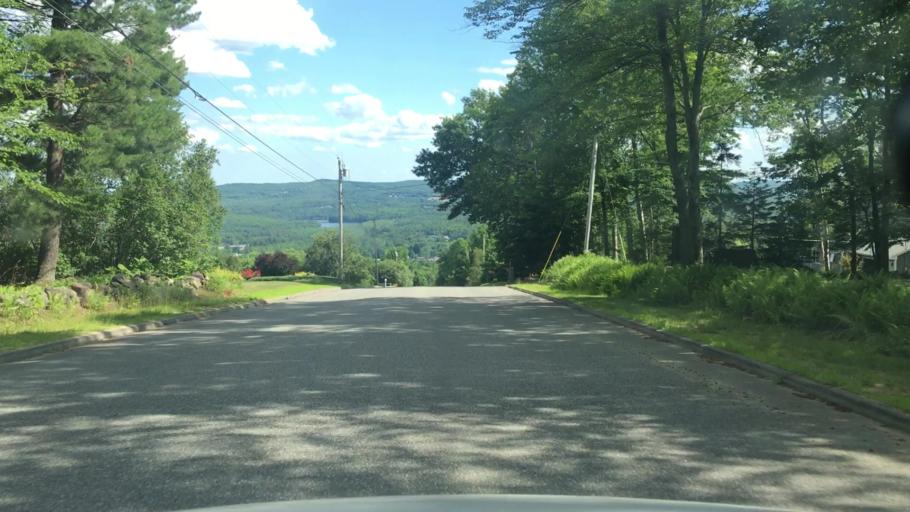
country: US
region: Maine
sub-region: Franklin County
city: Wilton
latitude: 44.6338
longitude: -70.1980
